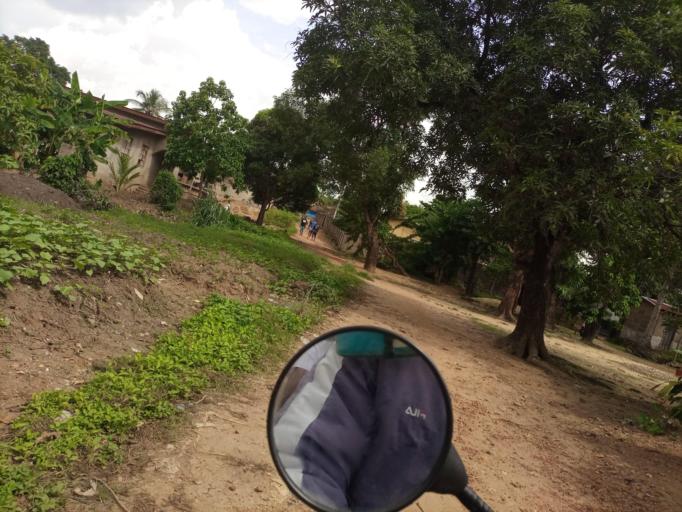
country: SL
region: Southern Province
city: Bo
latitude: 7.9454
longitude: -11.7331
